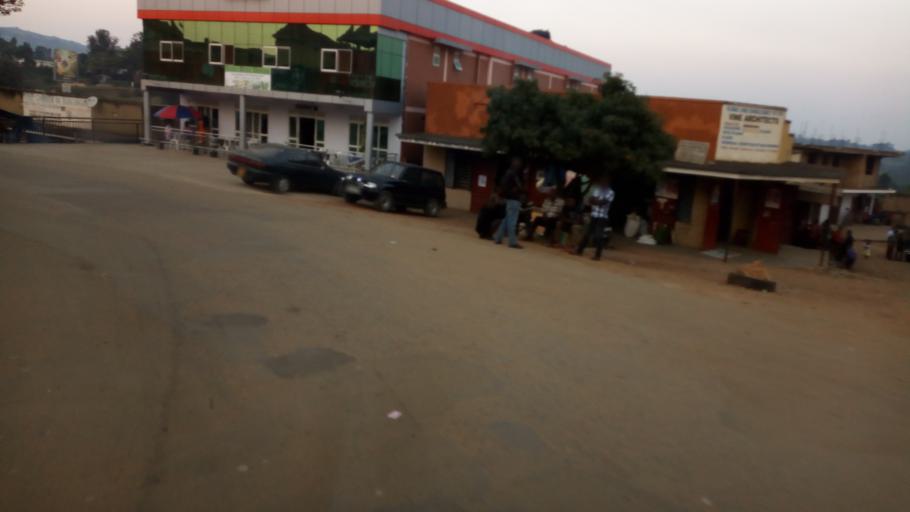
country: UG
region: Western Region
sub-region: Rukungiri District
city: Rukungiri
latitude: -0.7933
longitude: 29.9257
